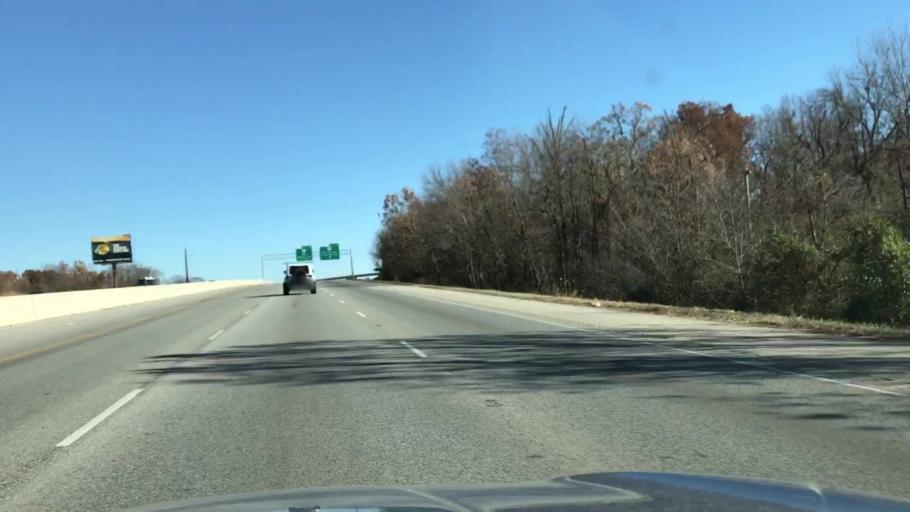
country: US
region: Arkansas
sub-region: Benton County
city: Bethel Heights
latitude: 36.2329
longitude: -94.1716
